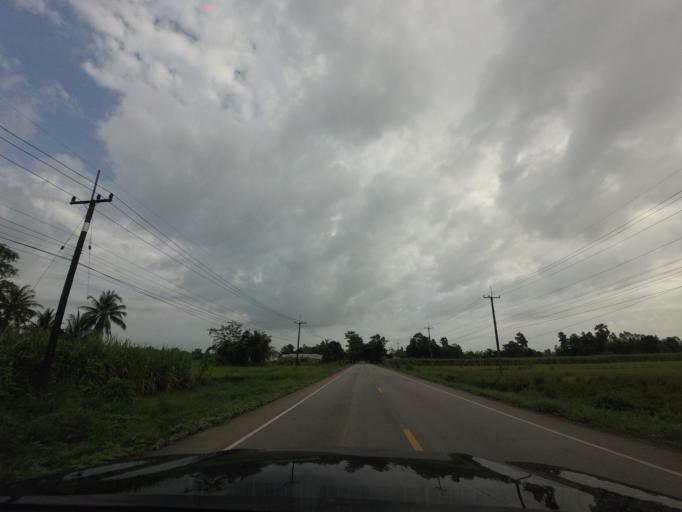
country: TH
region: Changwat Udon Thani
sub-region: Amphoe Ban Phue
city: Ban Phue
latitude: 17.7355
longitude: 102.3967
